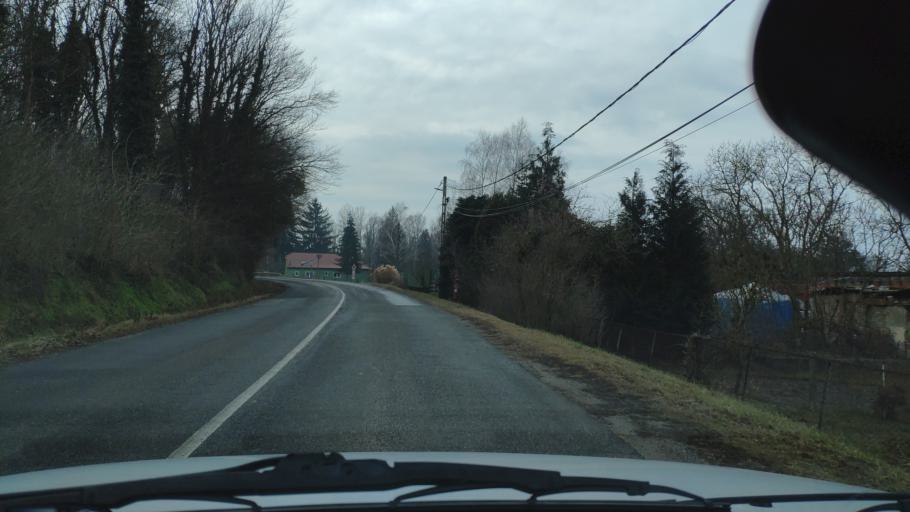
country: HU
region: Zala
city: Nagykanizsa
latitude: 46.5162
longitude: 16.9813
